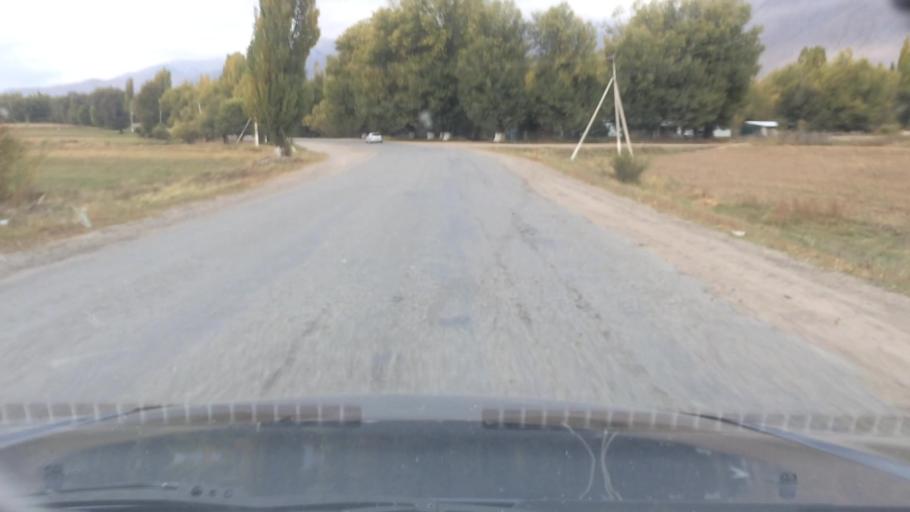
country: KG
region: Ysyk-Koel
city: Tyup
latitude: 42.7869
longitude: 78.2634
